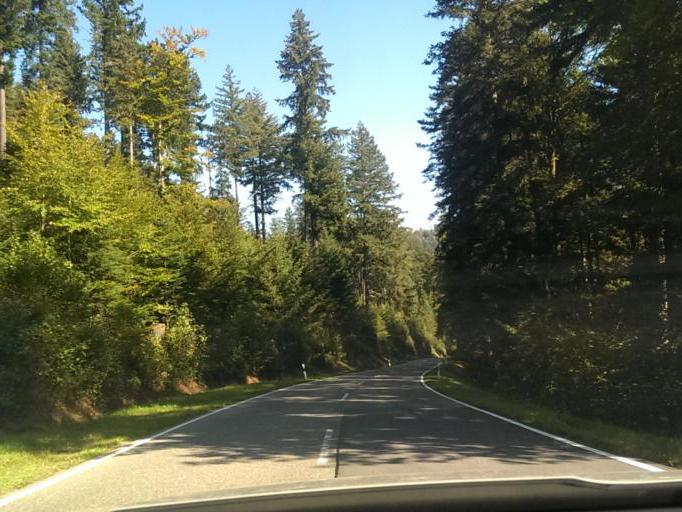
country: DE
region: Baden-Wuerttemberg
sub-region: Karlsruhe Region
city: Hofen an der Enz
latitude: 48.8147
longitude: 8.5685
